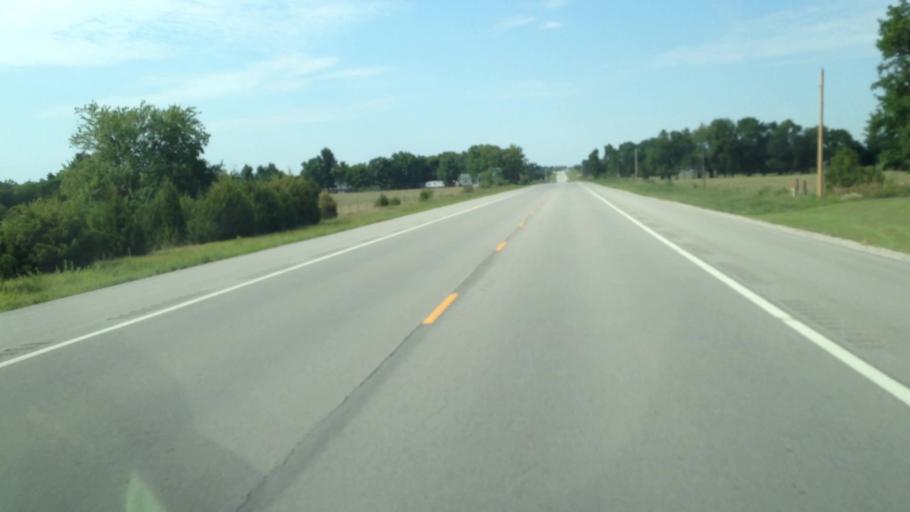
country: US
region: Kansas
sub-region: Labette County
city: Altamont
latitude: 37.2624
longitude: -95.2672
